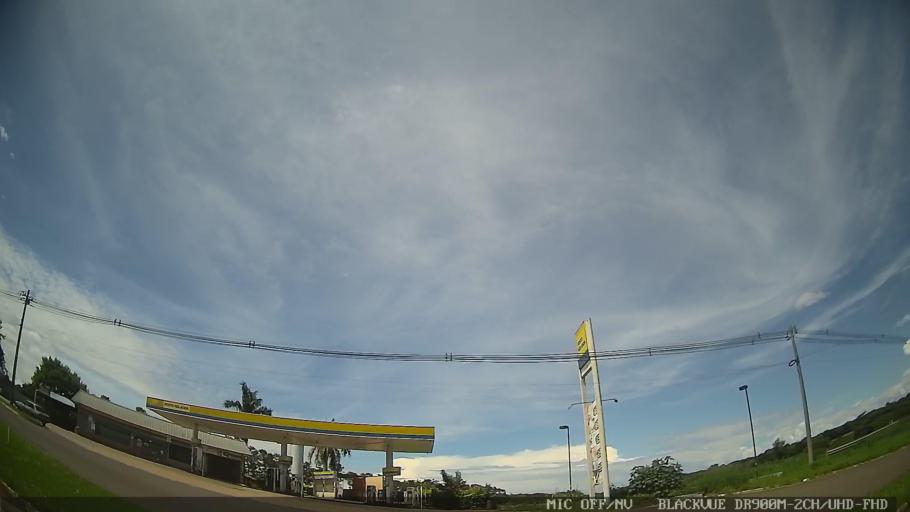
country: BR
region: Sao Paulo
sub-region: Jaguariuna
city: Jaguariuna
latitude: -22.6292
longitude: -47.0449
